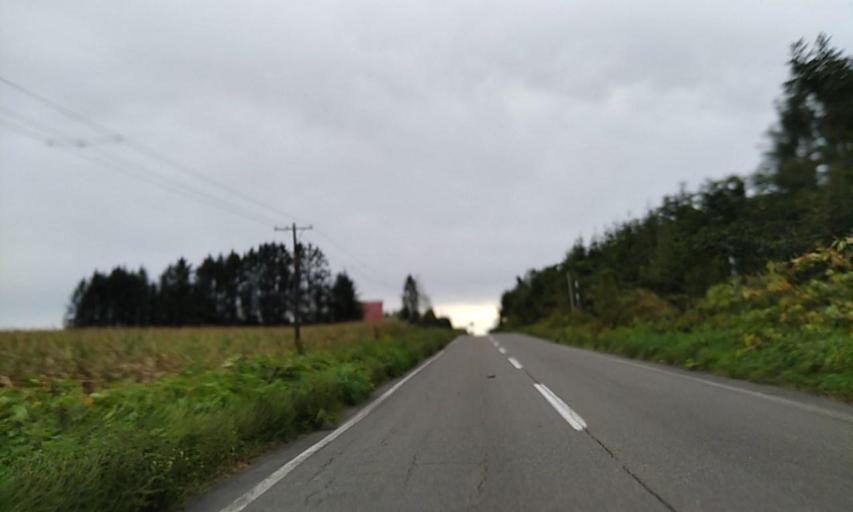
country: JP
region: Hokkaido
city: Obihiro
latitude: 42.6638
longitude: 143.0705
